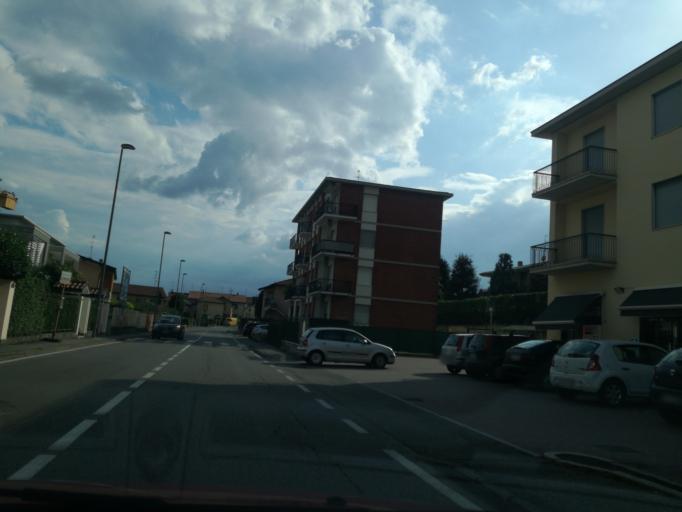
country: IT
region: Lombardy
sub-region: Provincia di Monza e Brianza
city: Villanova
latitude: 45.6241
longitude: 9.3852
